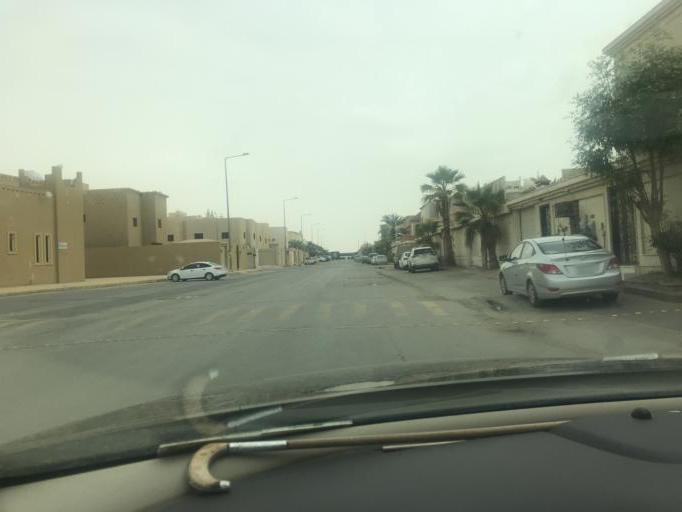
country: SA
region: Ar Riyad
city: Riyadh
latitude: 24.7365
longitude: 46.7883
